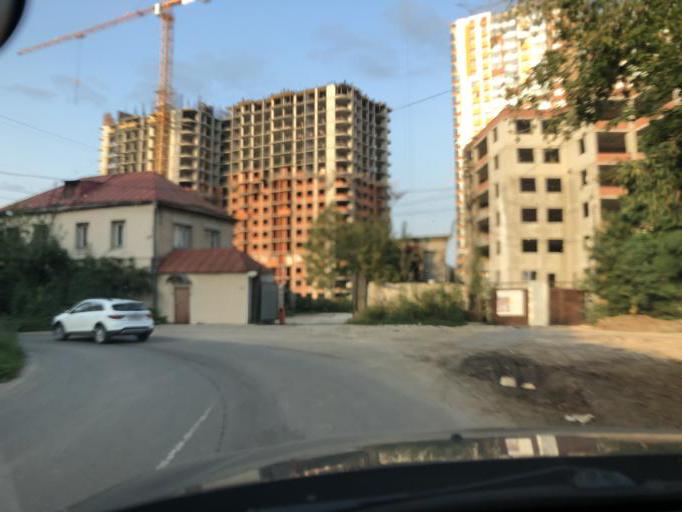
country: RU
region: Tula
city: Tula
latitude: 54.1743
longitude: 37.6289
